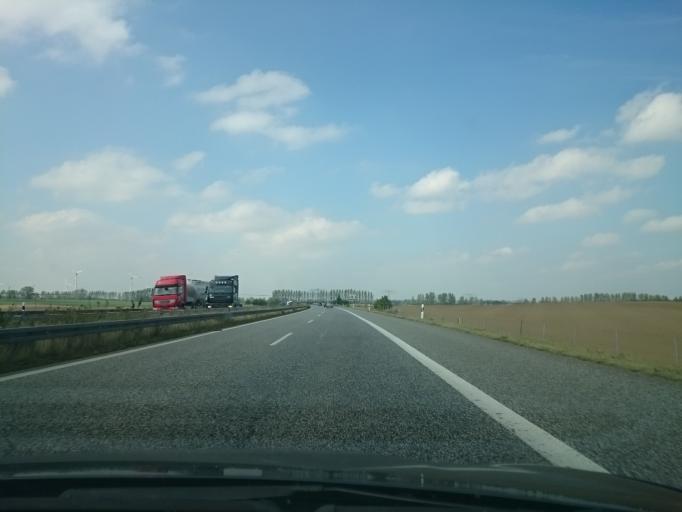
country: DE
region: Brandenburg
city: Schonfeld
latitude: 53.4407
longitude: 13.9916
